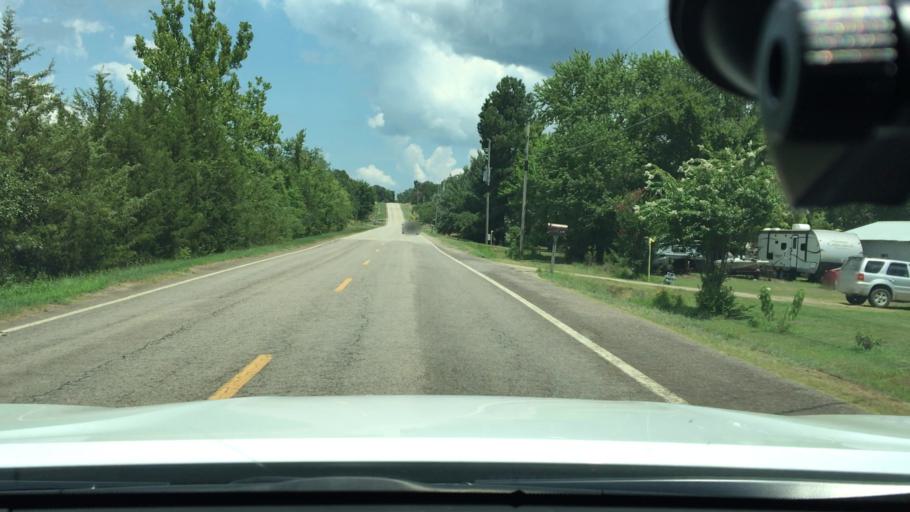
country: US
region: Arkansas
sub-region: Logan County
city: Booneville
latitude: 35.1516
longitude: -93.8770
